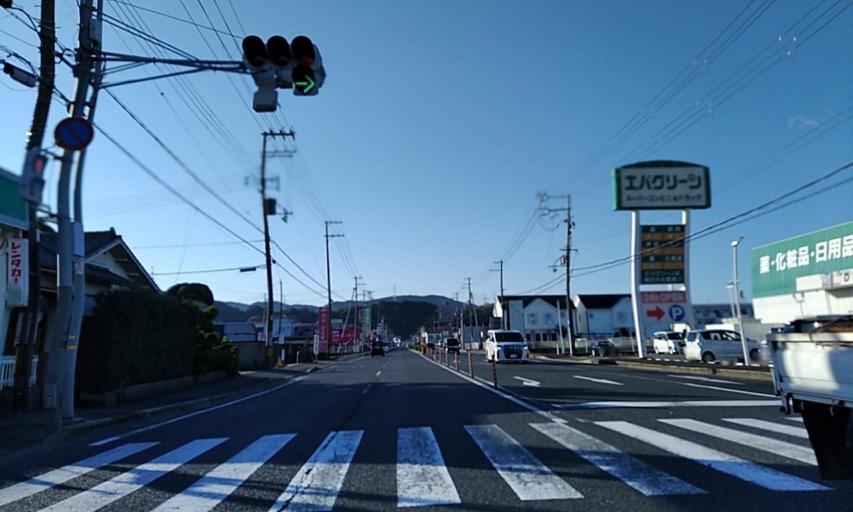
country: JP
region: Wakayama
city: Kainan
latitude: 34.1711
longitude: 135.1869
